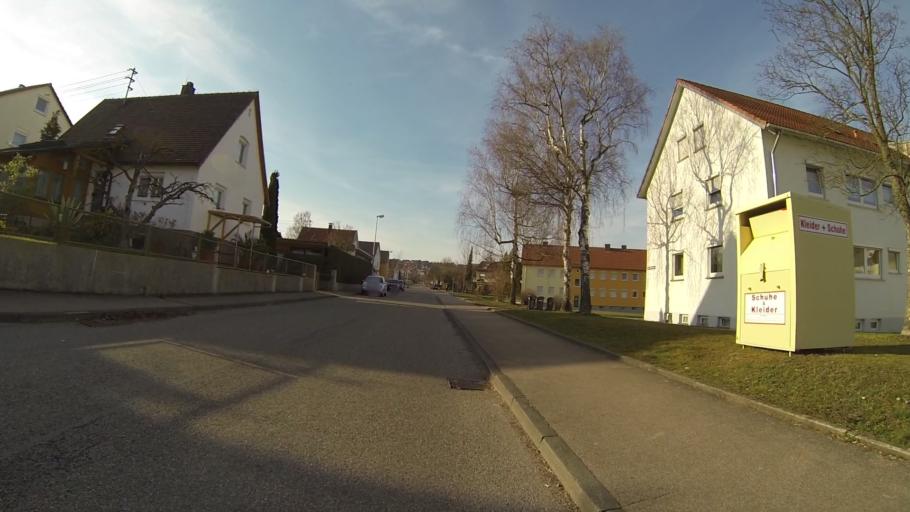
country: DE
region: Baden-Wuerttemberg
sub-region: Regierungsbezirk Stuttgart
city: Herbrechtingen
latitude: 48.6260
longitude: 10.1800
